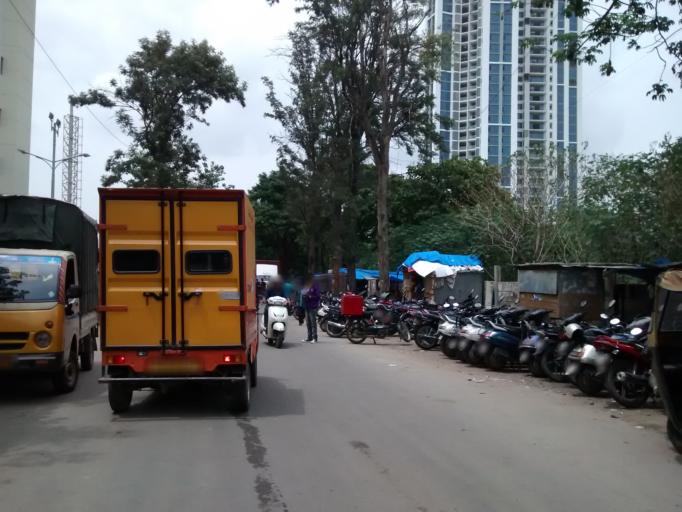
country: IN
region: Karnataka
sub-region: Bangalore Urban
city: Bangalore
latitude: 12.8755
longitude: 77.5959
